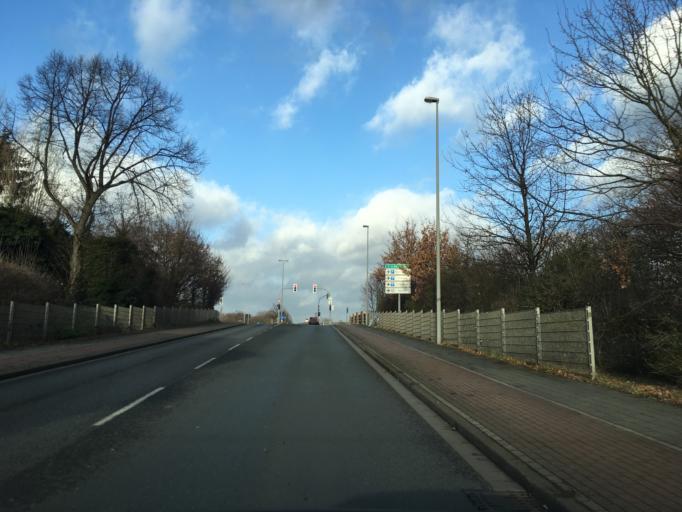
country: DE
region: North Rhine-Westphalia
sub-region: Regierungsbezirk Dusseldorf
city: Oberhausen
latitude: 51.5131
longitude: 6.8425
